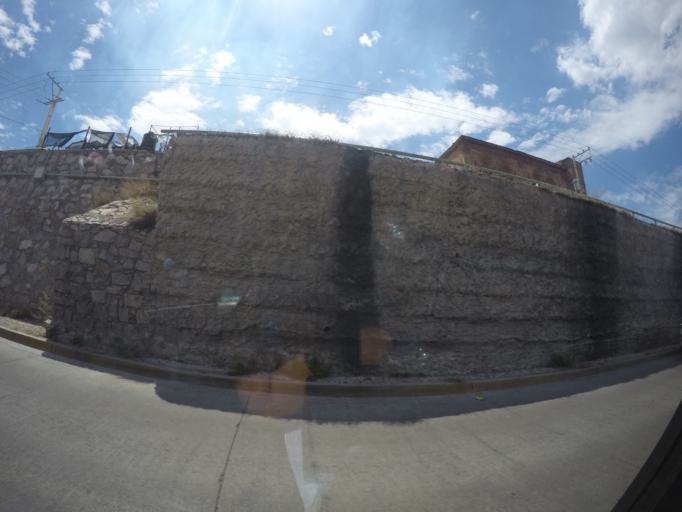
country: MX
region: Guanajuato
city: Leon
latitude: 21.1288
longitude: -101.6769
